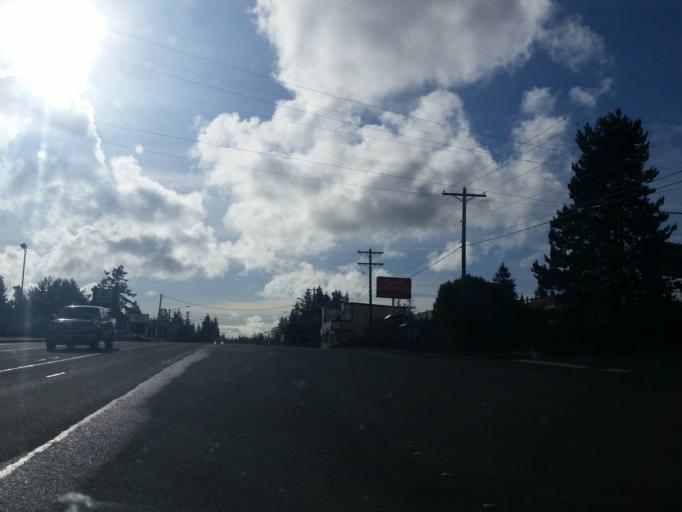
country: US
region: Washington
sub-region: Snohomish County
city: Esperance
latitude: 47.7907
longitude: -122.3381
